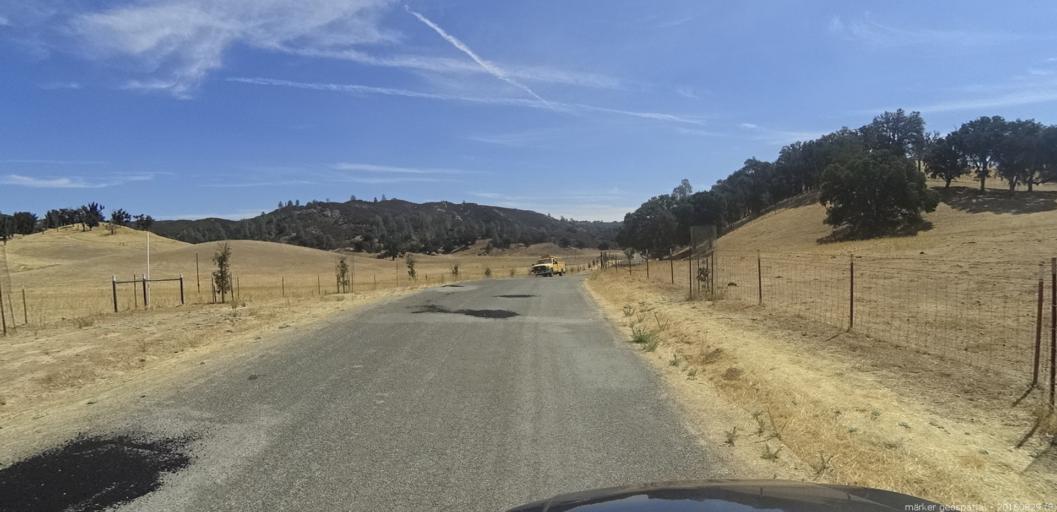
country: US
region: California
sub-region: San Luis Obispo County
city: Lake Nacimiento
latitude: 35.8147
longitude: -121.0987
